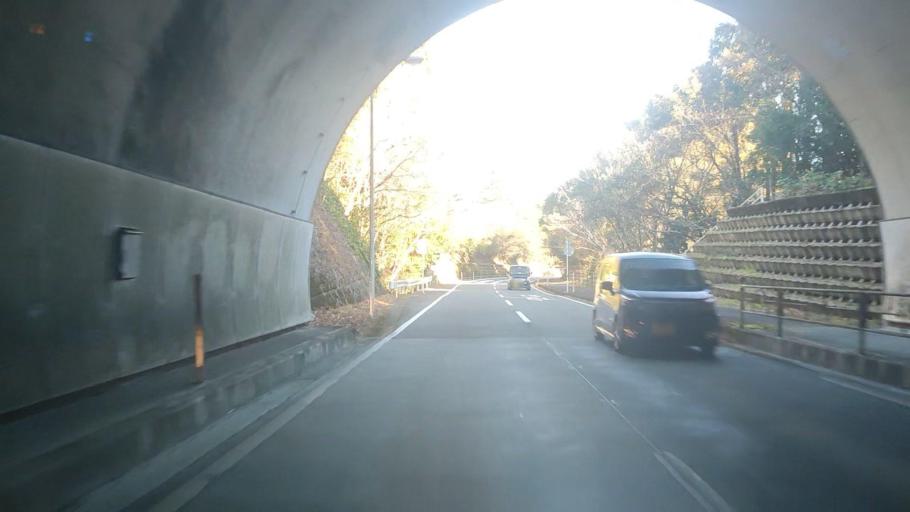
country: JP
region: Miyazaki
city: Nobeoka
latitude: 32.7034
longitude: 131.8157
